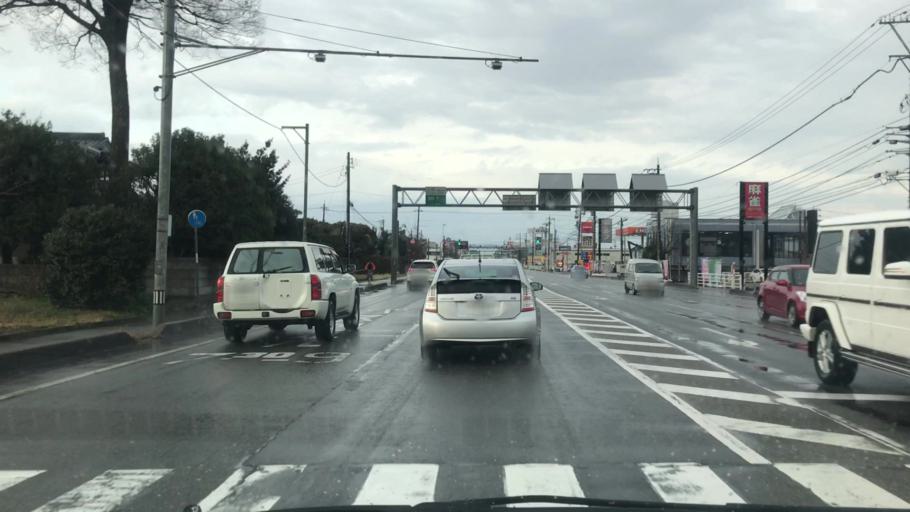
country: JP
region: Toyama
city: Toyama-shi
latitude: 36.6434
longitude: 137.2095
